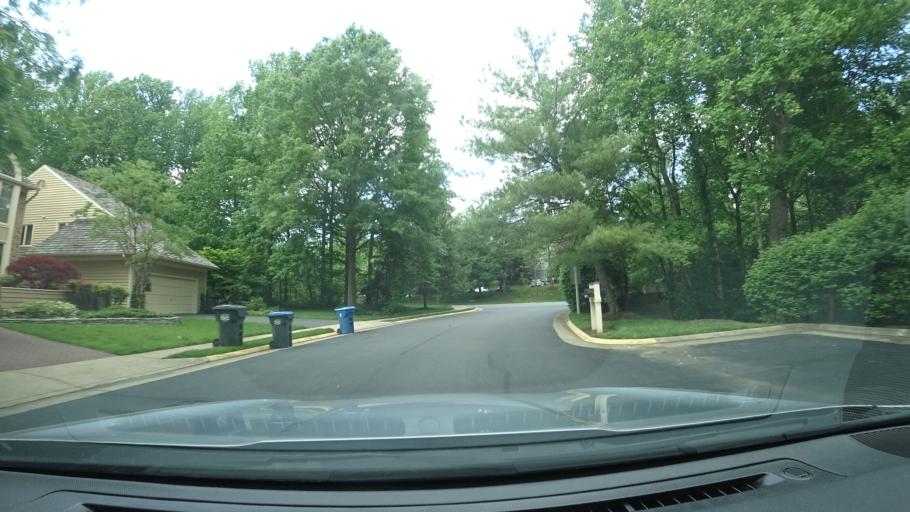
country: US
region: Virginia
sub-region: Fairfax County
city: Reston
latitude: 38.9772
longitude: -77.3414
